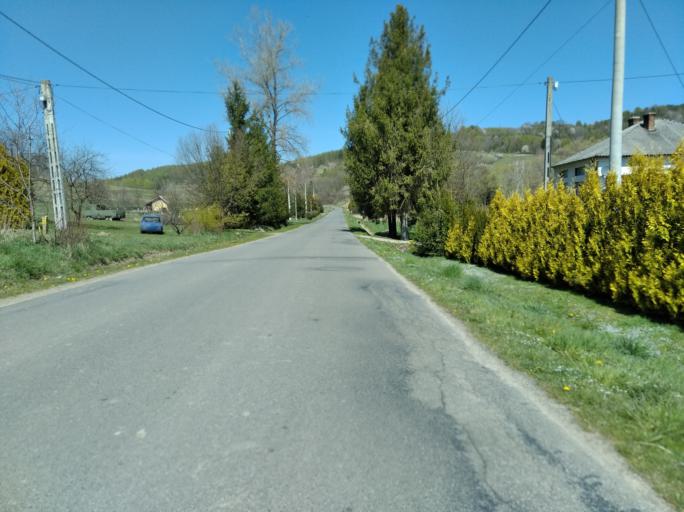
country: PL
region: Subcarpathian Voivodeship
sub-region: Powiat brzozowski
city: Dydnia
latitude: 49.6992
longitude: 22.1523
